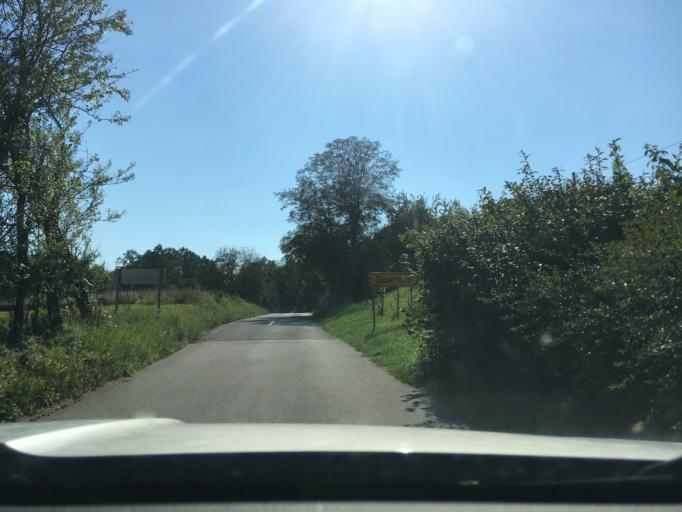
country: SI
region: Crnomelj
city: Crnomelj
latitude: 45.4574
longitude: 15.2449
